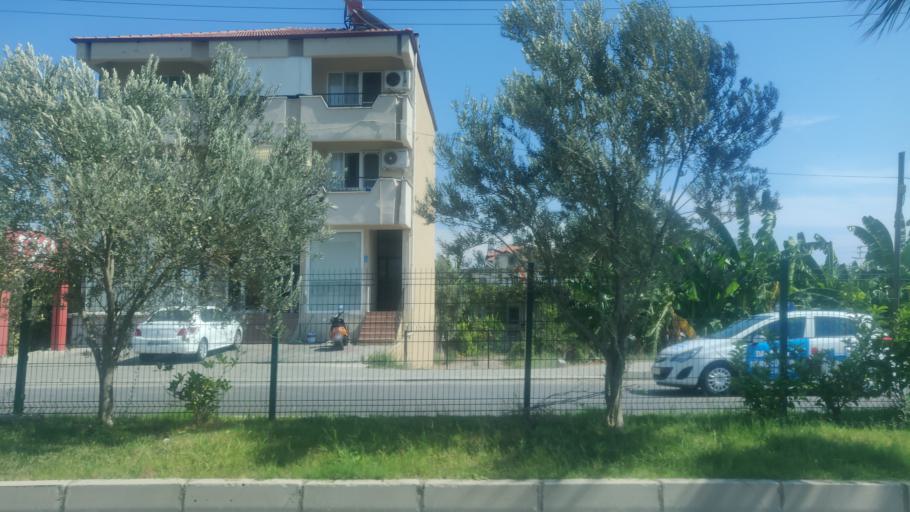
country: TR
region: Mugla
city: Dalaman
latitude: 36.7761
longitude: 28.8012
